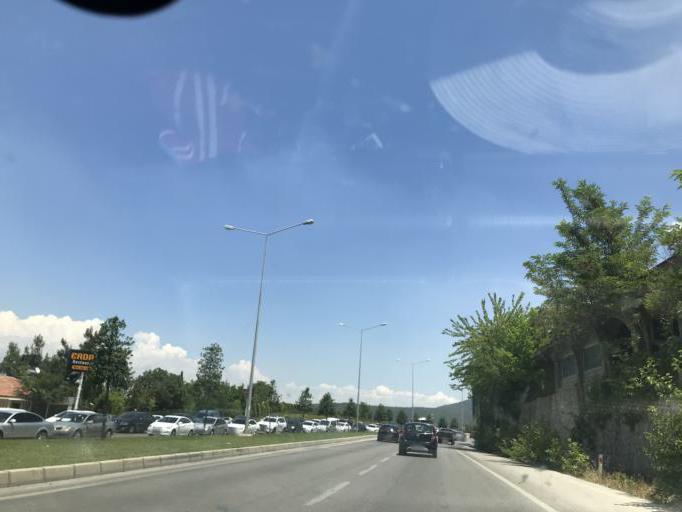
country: TR
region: Denizli
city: Denizli
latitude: 37.7309
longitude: 29.1566
